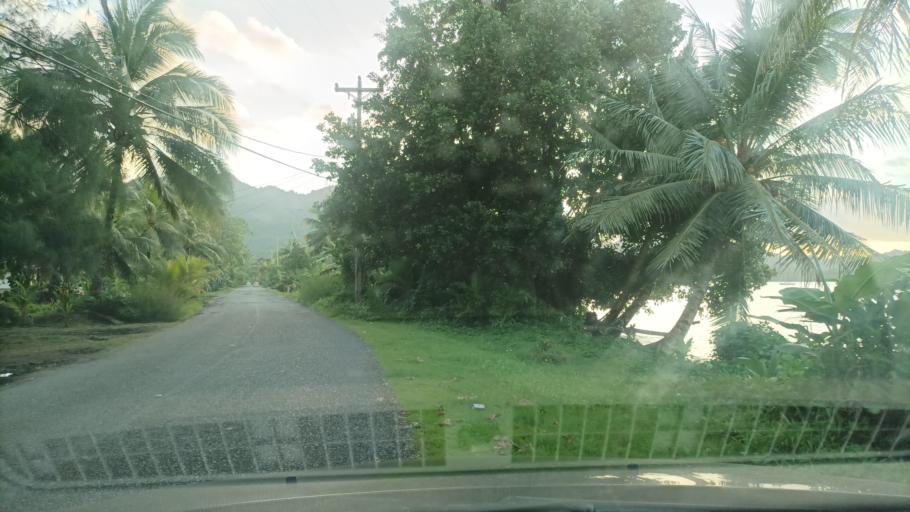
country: FM
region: Kosrae
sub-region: Lelu Municipality
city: Lelu
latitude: 5.3215
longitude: 163.0291
